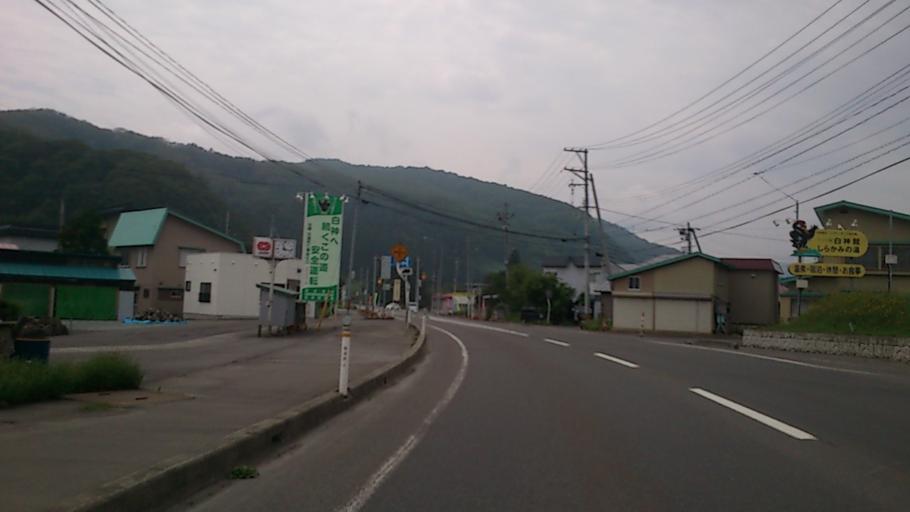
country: JP
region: Aomori
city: Hirosaki
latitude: 40.5775
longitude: 140.2993
